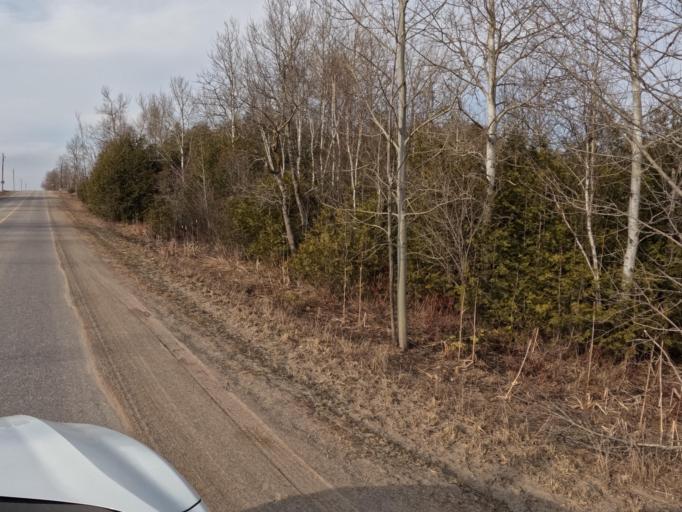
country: CA
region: Ontario
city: Orangeville
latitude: 43.8891
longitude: -80.2652
